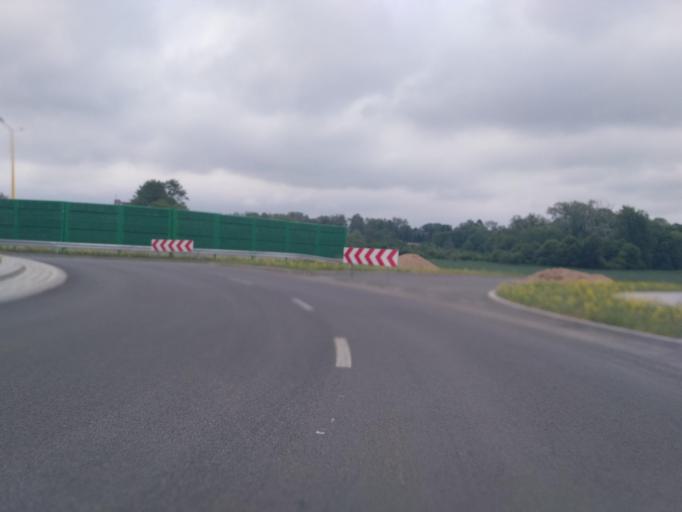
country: PL
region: Subcarpathian Voivodeship
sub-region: Krosno
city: Krosno
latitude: 49.6752
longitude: 21.7624
